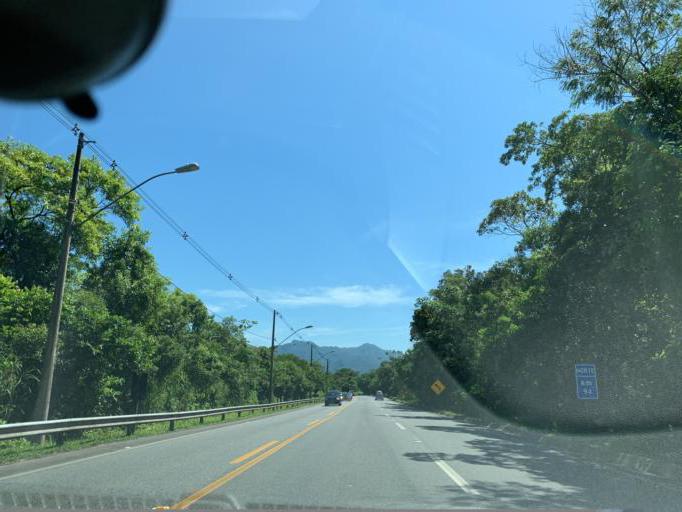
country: BR
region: Sao Paulo
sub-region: Bertioga
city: Bertioga
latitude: -23.7679
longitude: -46.0389
